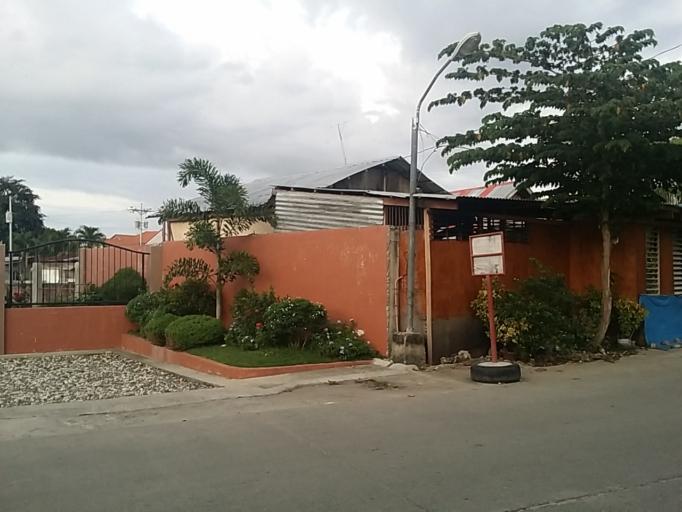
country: PH
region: Central Visayas
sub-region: Province of Cebu
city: Bogo
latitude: 11.0493
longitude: 124.0063
